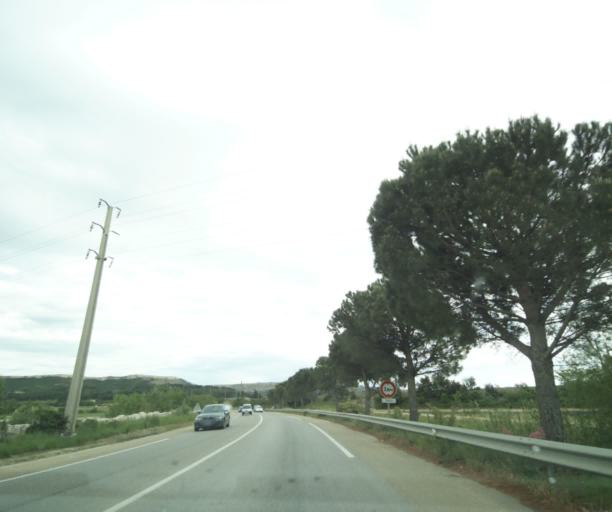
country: FR
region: Provence-Alpes-Cote d'Azur
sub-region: Departement des Bouches-du-Rhone
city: Rognac
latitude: 43.5034
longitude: 5.2218
